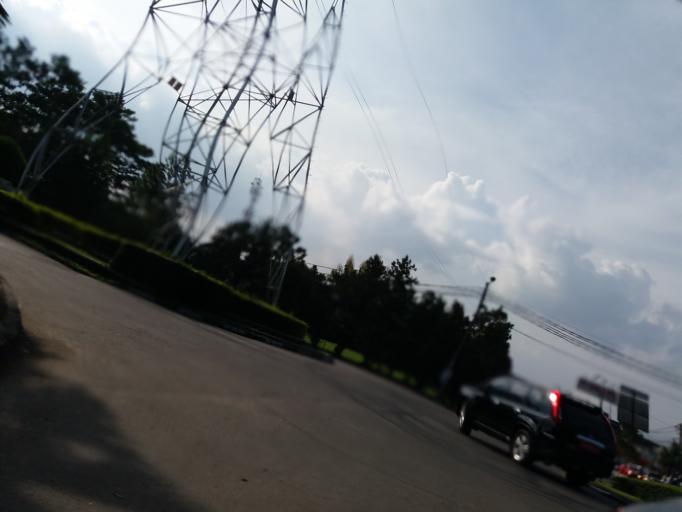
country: ID
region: West Java
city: Bandung
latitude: -6.9541
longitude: 107.6273
